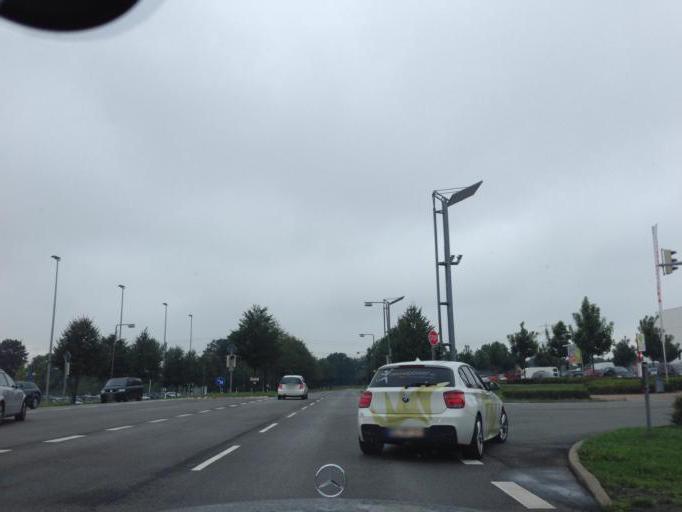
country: DE
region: Schleswig-Holstein
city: Barsbuettel
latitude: 53.5771
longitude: 10.1950
